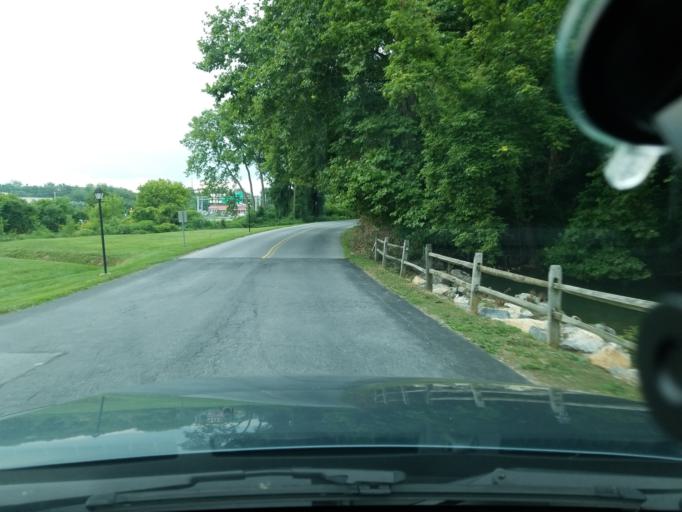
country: US
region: Pennsylvania
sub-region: Dauphin County
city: Hummelstown
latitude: 40.2679
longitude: -76.6871
